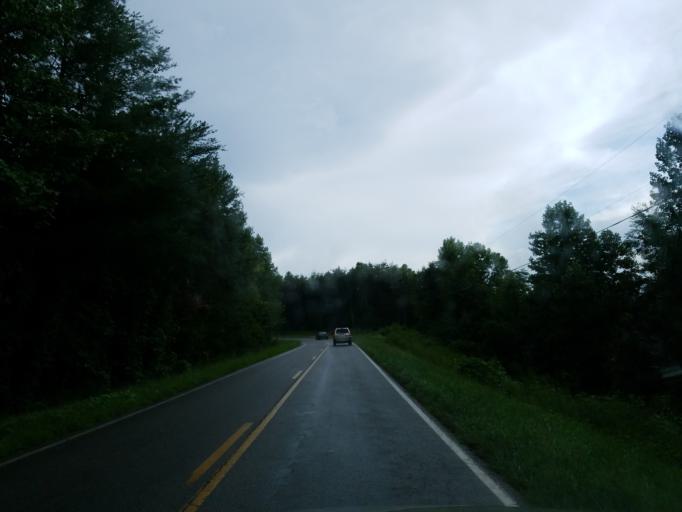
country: US
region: Georgia
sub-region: Lumpkin County
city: Dahlonega
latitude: 34.5503
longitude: -83.8835
